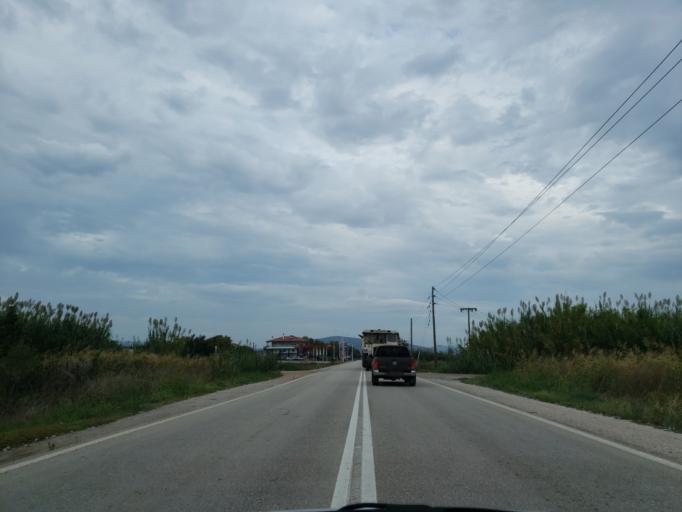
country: GR
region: Central Greece
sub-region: Nomos Voiotias
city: Orchomenos
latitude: 38.4889
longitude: 22.9829
